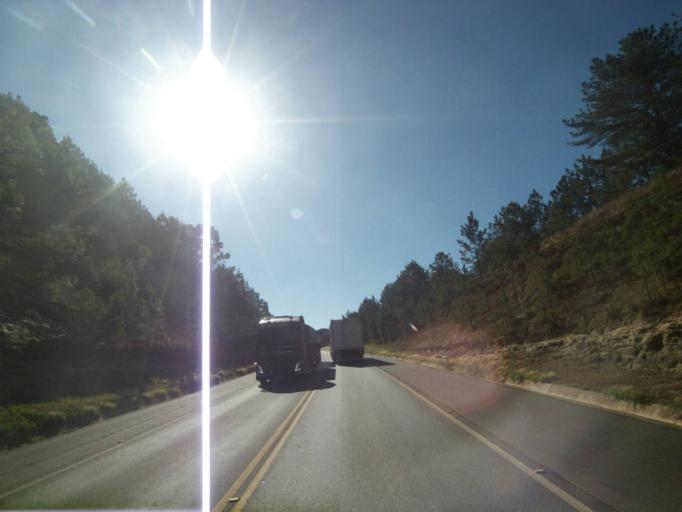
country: BR
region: Parana
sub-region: Tibagi
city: Tibagi
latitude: -24.5853
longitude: -50.4371
